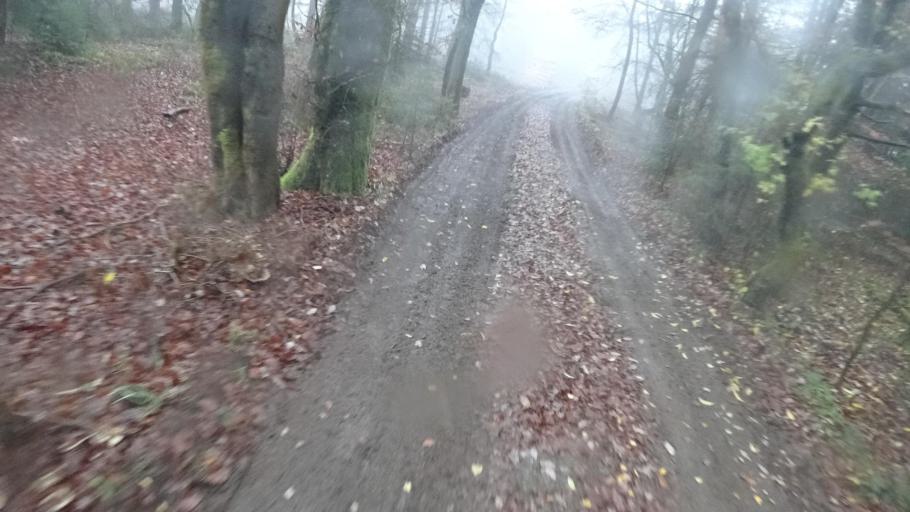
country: DE
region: Rheinland-Pfalz
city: Karbach
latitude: 50.1709
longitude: 7.6033
